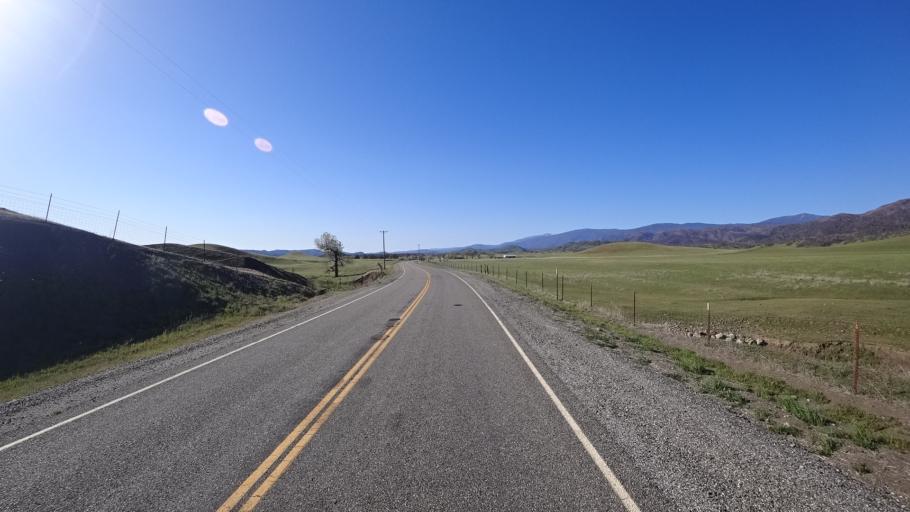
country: US
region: California
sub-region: Tehama County
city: Rancho Tehama Reserve
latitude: 39.7083
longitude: -122.5504
